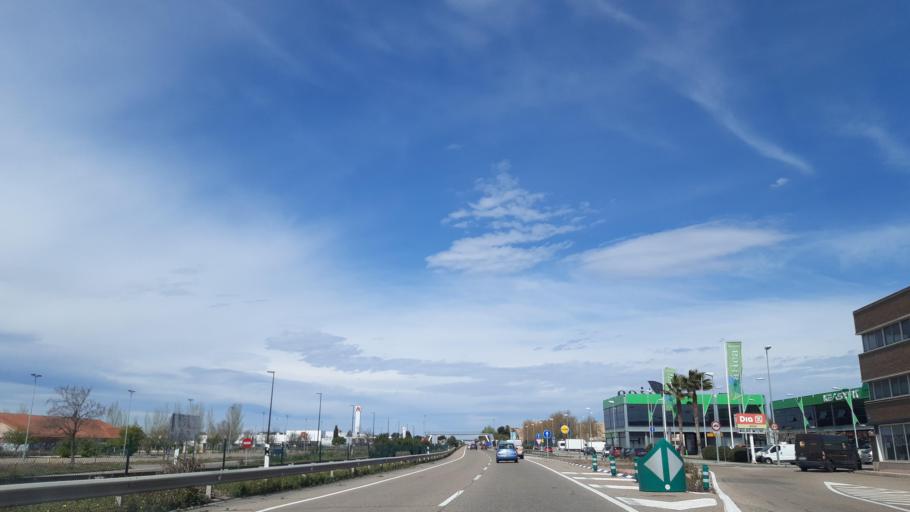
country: ES
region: Aragon
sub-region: Provincia de Zaragoza
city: Utebo
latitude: 41.7000
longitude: -0.9963
